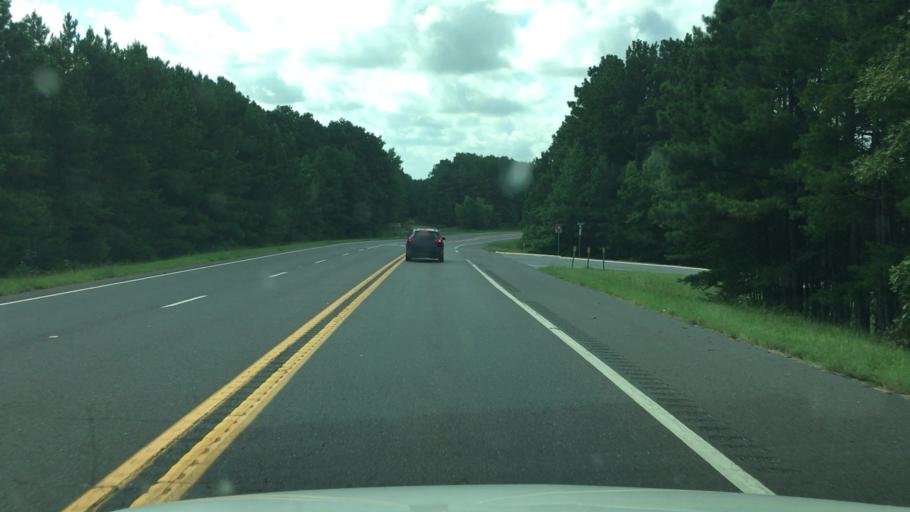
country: US
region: Arkansas
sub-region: Clark County
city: Arkadelphia
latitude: 34.2108
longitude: -93.0807
